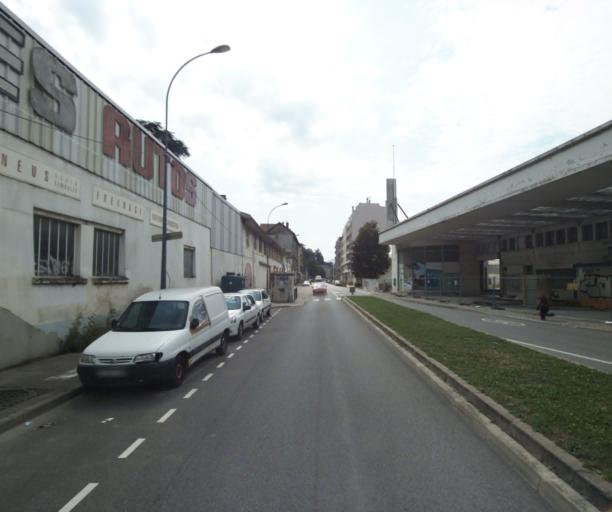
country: FR
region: Rhone-Alpes
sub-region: Departement de l'Isere
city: Saint-Martin-le-Vinoux
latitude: 45.1980
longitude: 5.7184
